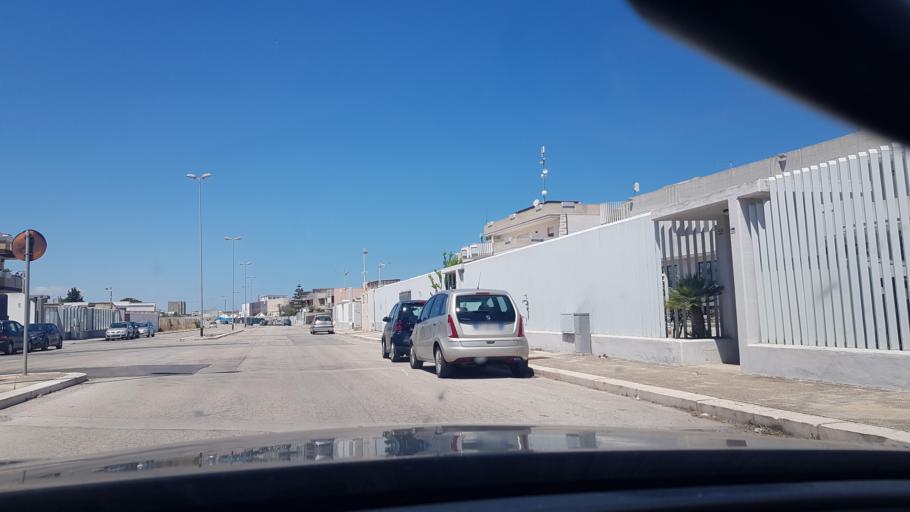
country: IT
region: Apulia
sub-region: Provincia di Barletta - Andria - Trani
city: Barletta
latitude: 41.3061
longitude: 16.3228
